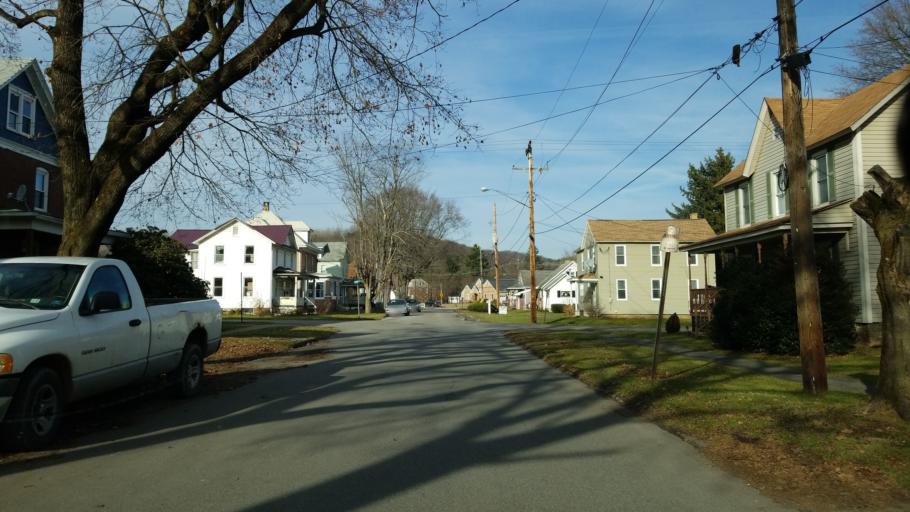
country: US
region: Pennsylvania
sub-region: Clearfield County
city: Clearfield
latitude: 41.0307
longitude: -78.4417
